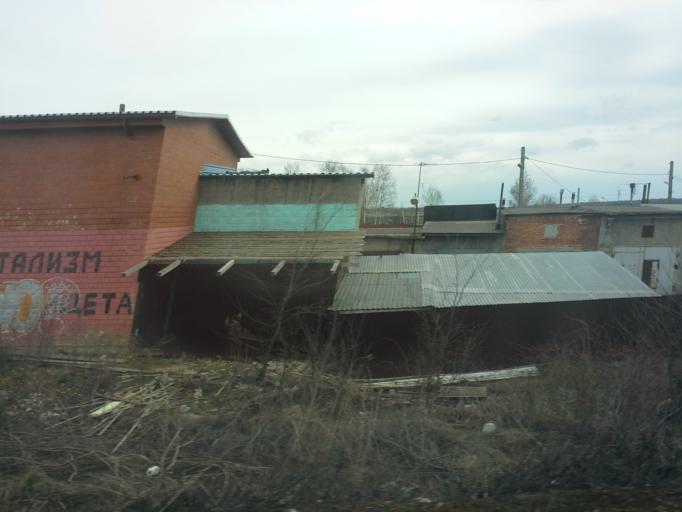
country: RU
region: Moskovskaya
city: Sergiyev Posad
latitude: 56.2893
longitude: 38.1167
